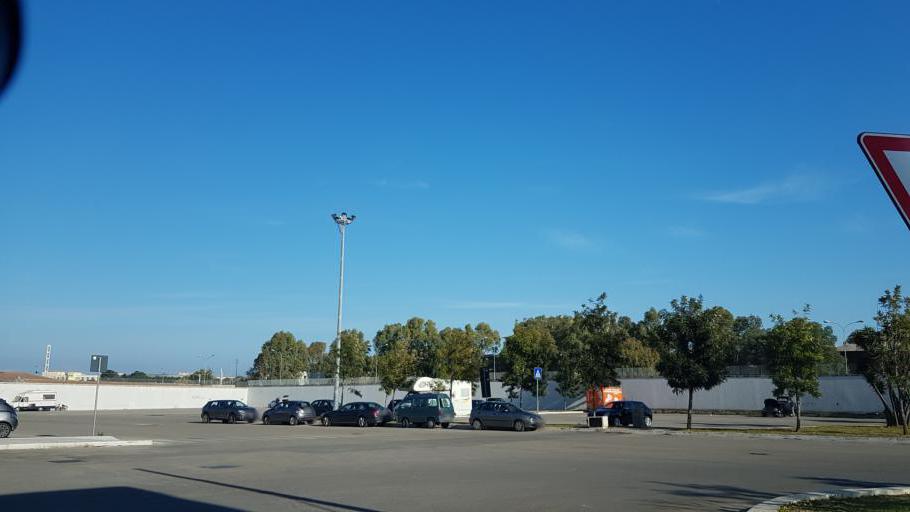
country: IT
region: Apulia
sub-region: Provincia di Brindisi
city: Brindisi
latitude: 40.6323
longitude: 17.9471
